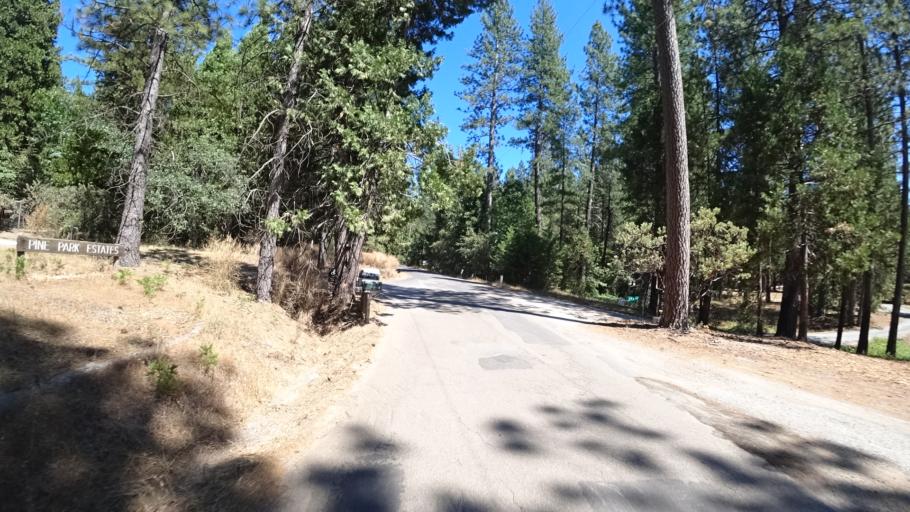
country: US
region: California
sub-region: Calaveras County
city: Mountain Ranch
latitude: 38.2824
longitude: -120.5446
